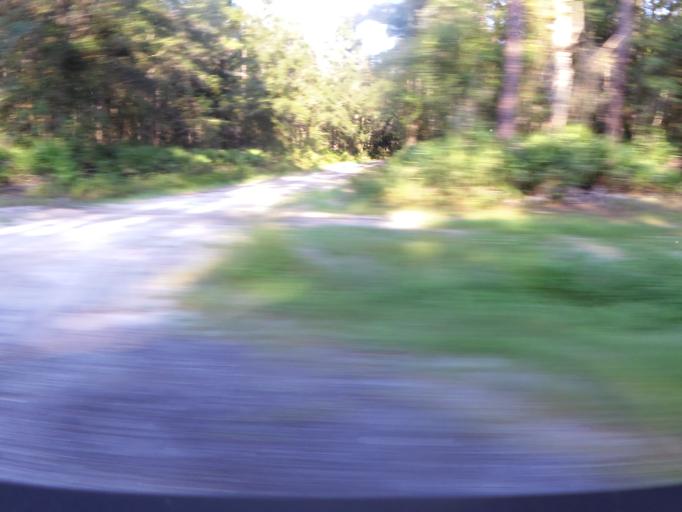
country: US
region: Florida
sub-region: Duval County
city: Baldwin
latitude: 30.3979
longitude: -82.0314
